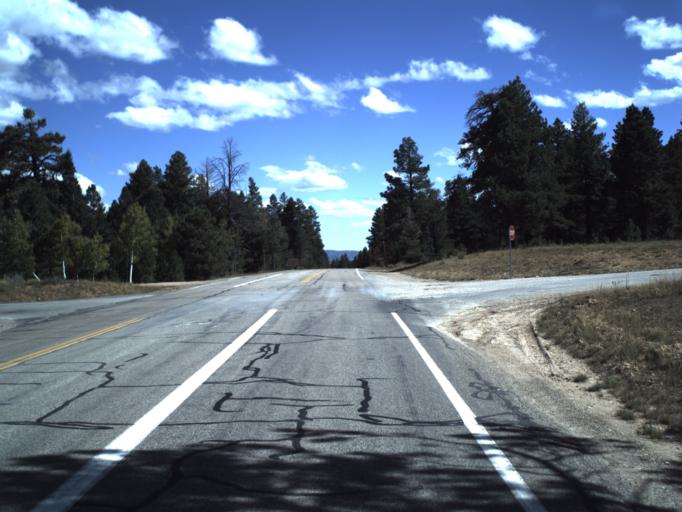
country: US
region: Utah
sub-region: Garfield County
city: Panguitch
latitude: 37.5179
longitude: -112.6467
